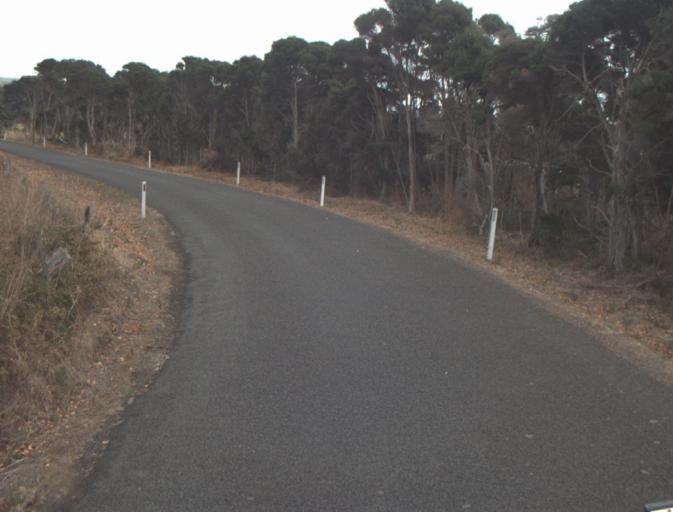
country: AU
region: Tasmania
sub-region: Launceston
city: Mayfield
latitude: -41.2893
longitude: 146.9912
